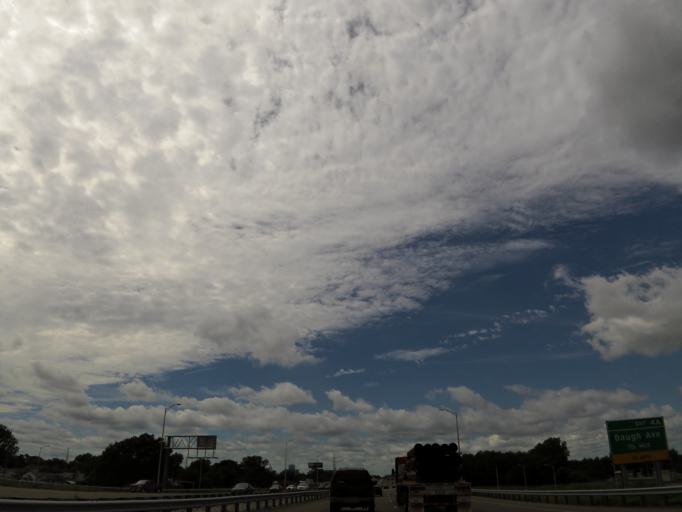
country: US
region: Illinois
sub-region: Saint Clair County
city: East Saint Louis
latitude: 38.6218
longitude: -90.1221
